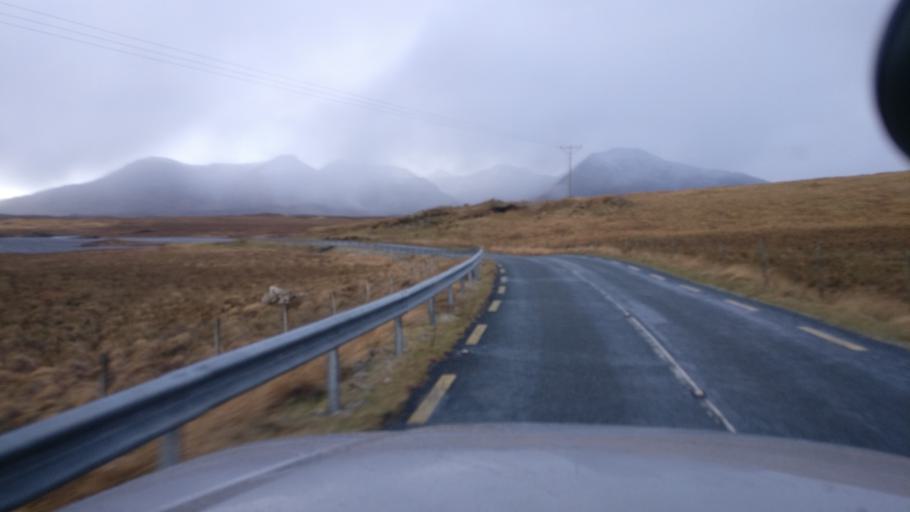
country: IE
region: Connaught
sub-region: County Galway
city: Clifden
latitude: 53.4378
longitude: -9.7689
